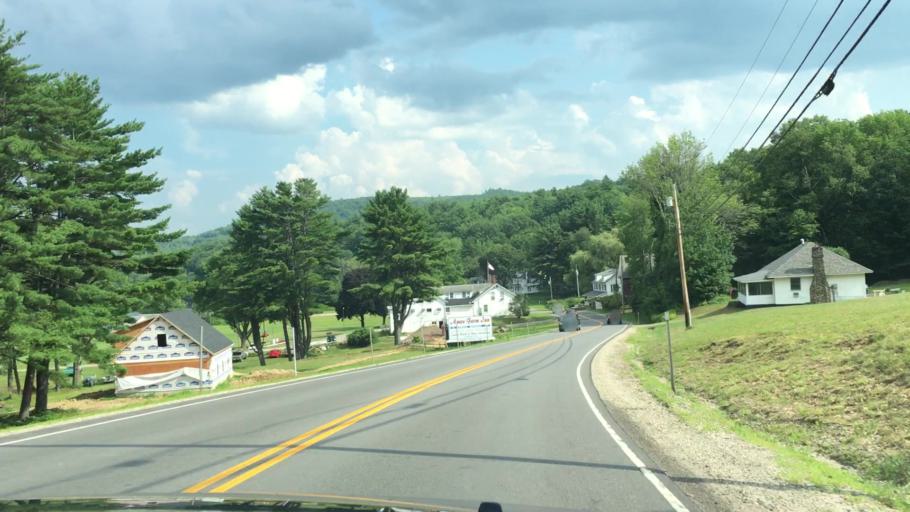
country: US
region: New Hampshire
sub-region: Belknap County
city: Gilford
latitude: 43.5646
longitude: -71.3363
